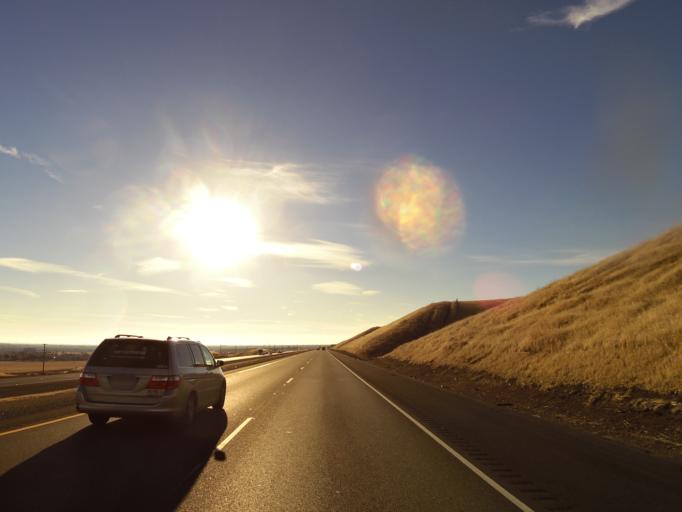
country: US
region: California
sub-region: Stanislaus County
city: Patterson
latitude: 37.4705
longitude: -121.1875
